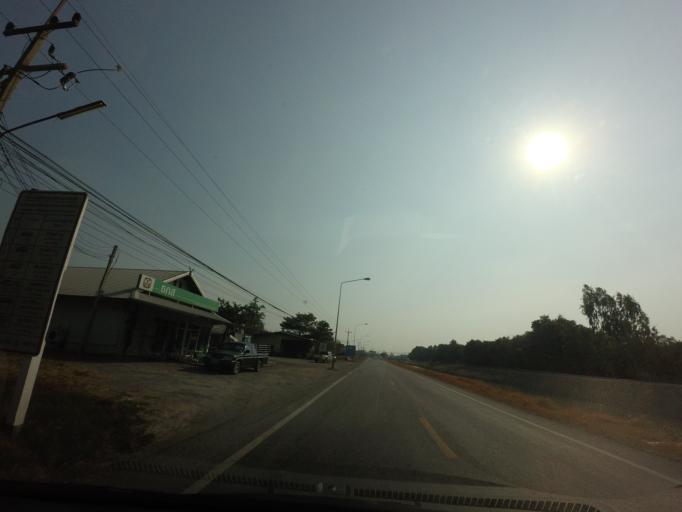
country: TH
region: Chachoengsao
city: Khlong Khuean
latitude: 13.7724
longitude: 101.1714
